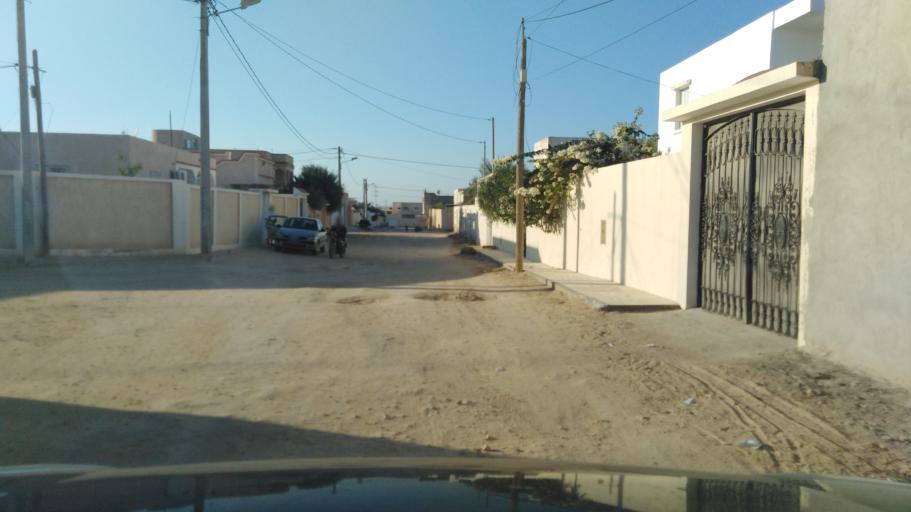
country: TN
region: Qabis
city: Gabes
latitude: 33.9515
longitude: 10.0125
